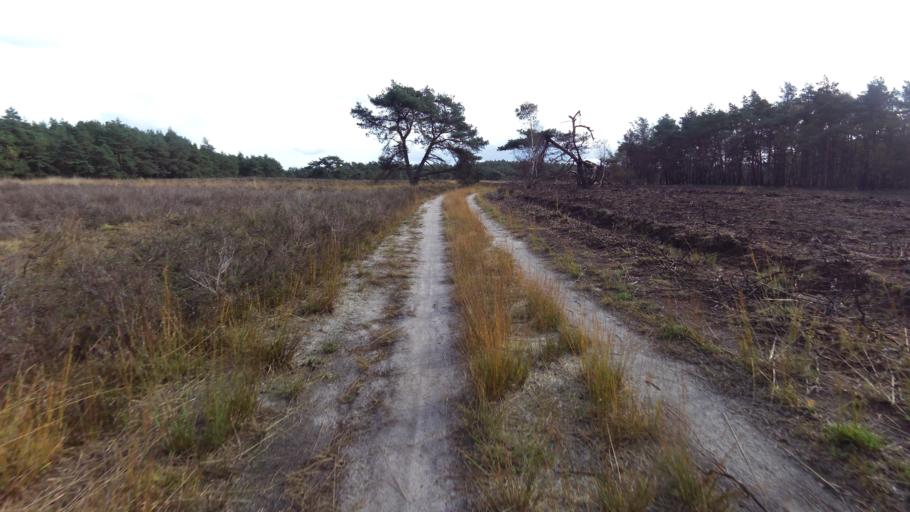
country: NL
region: Gelderland
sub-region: Gemeente Epe
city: Emst
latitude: 52.3376
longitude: 5.8959
